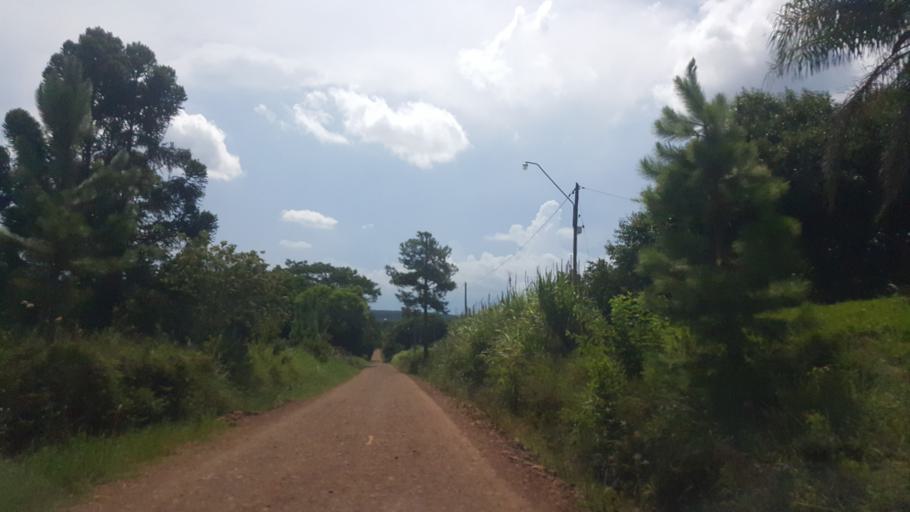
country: AR
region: Misiones
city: Capiovi
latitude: -26.9257
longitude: -55.0445
